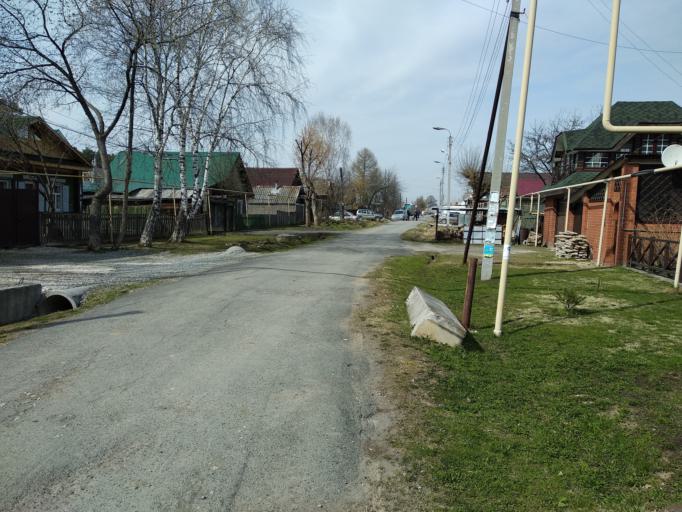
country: RU
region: Sverdlovsk
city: Beryozovsky
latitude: 56.9036
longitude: 60.7647
